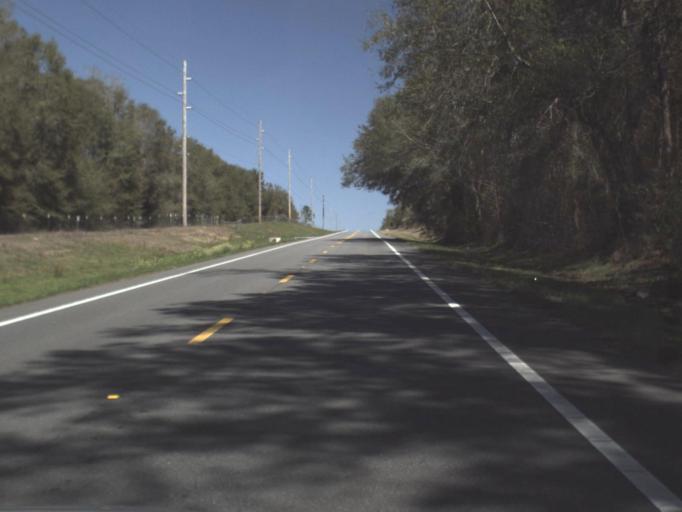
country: US
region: Florida
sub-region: Gadsden County
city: Quincy
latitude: 30.4518
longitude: -84.6427
